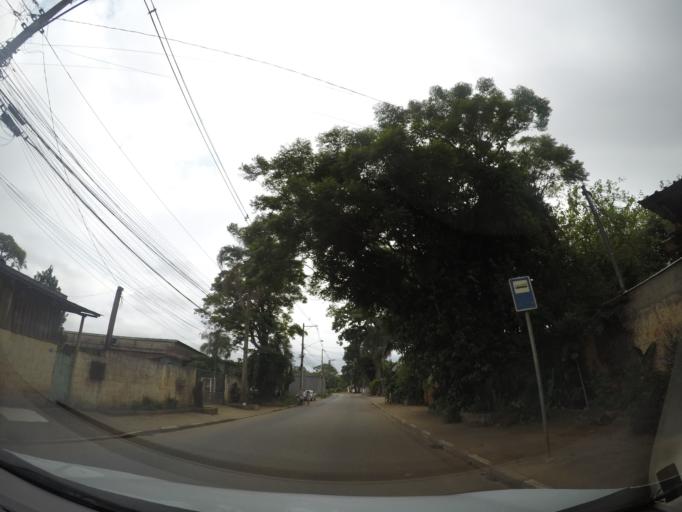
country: BR
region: Sao Paulo
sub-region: Aruja
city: Aruja
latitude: -23.3939
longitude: -46.3976
